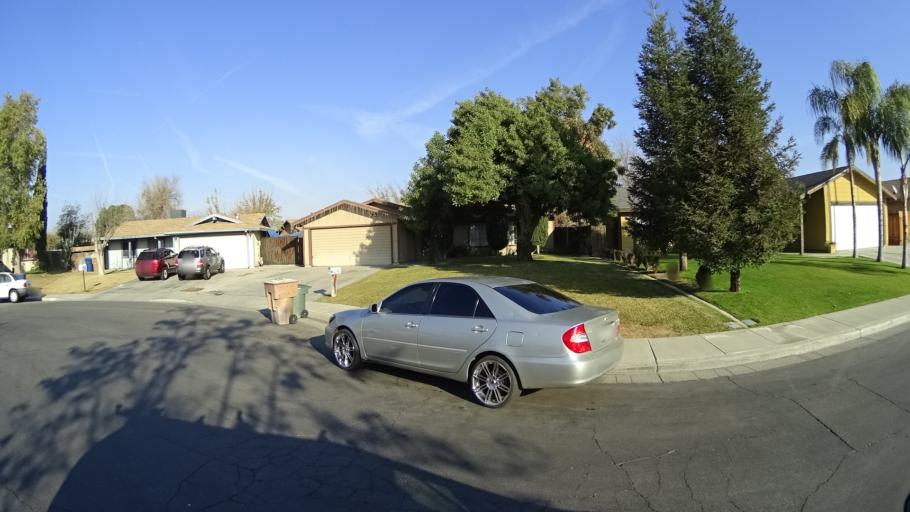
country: US
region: California
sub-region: Kern County
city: Greenfield
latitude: 35.3086
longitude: -119.0135
